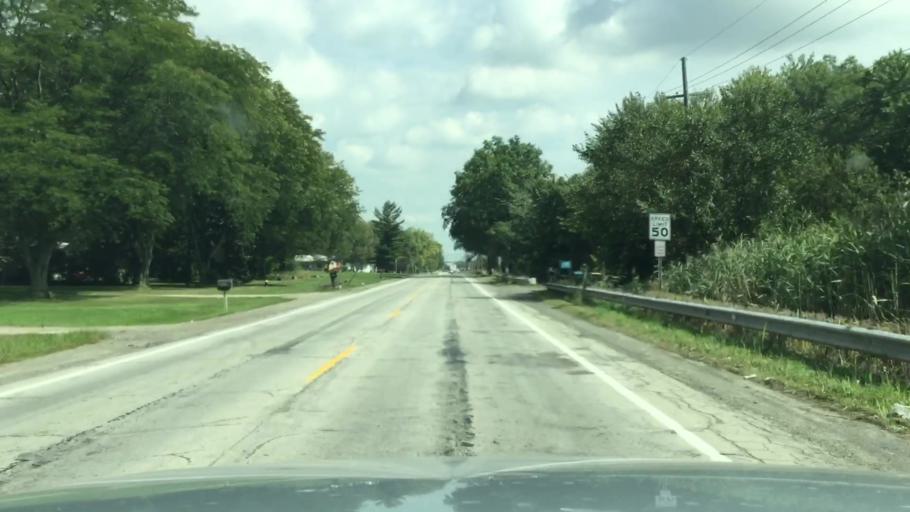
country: US
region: Michigan
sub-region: Wayne County
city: Wayne
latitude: 42.2523
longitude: -83.3741
